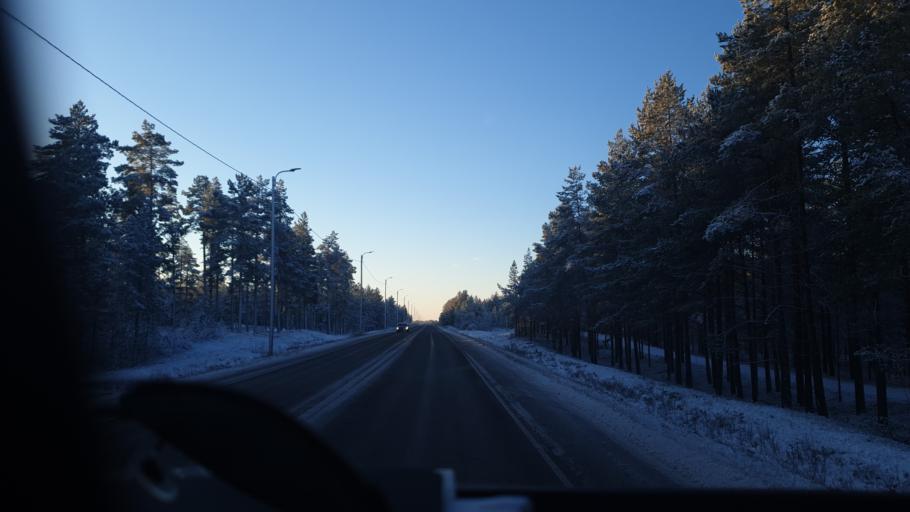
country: FI
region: Northern Ostrobothnia
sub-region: Ylivieska
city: Kalajoki
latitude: 64.2374
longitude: 23.8337
